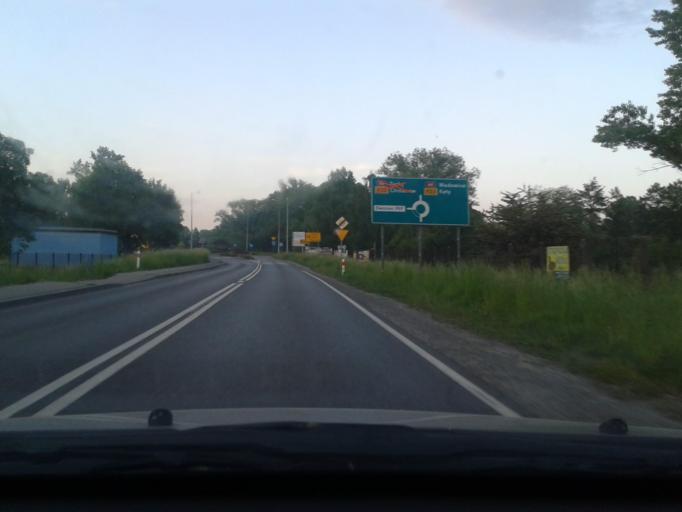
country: PL
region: Lesser Poland Voivodeship
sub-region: Powiat oswiecimski
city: Rajsko
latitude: 50.0215
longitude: 19.1993
